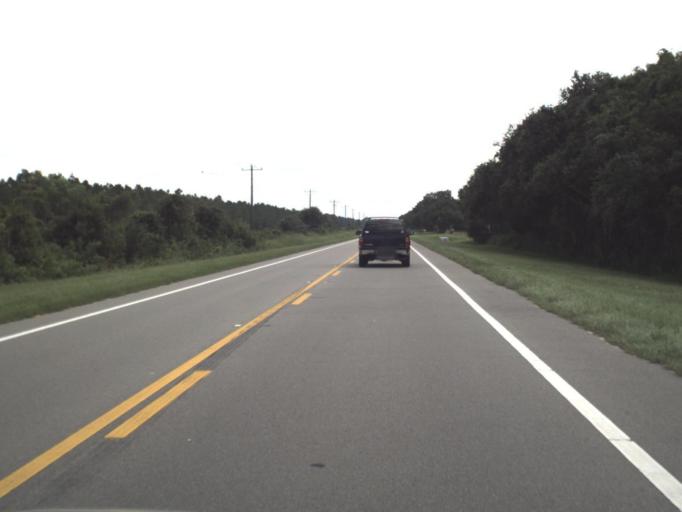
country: US
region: Florida
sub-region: Hillsborough County
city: Wimauma
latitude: 27.6022
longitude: -82.3150
